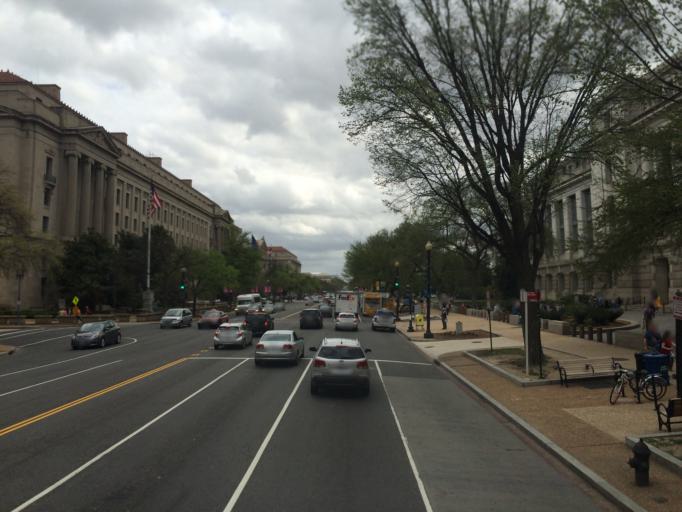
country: US
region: Washington, D.C.
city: Washington, D.C.
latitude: 38.8920
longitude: -77.0267
